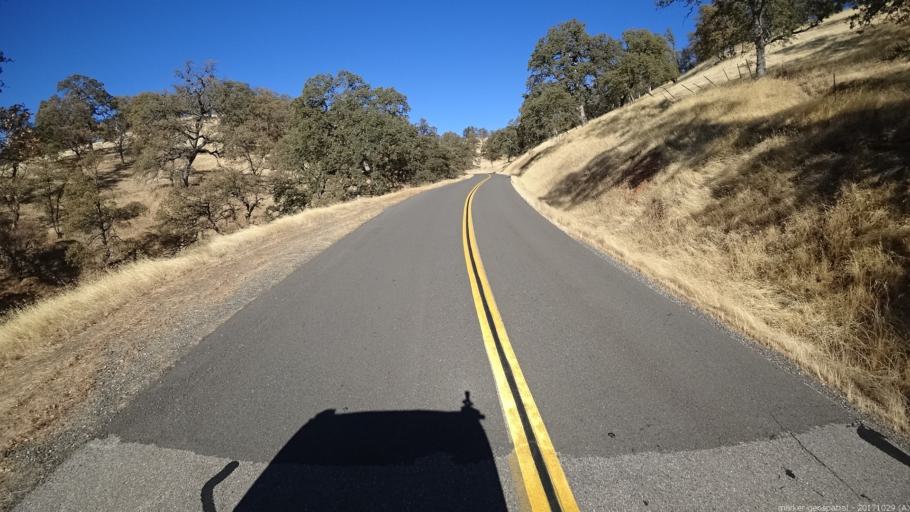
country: US
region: California
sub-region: Shasta County
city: Shasta
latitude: 40.4406
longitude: -122.6681
